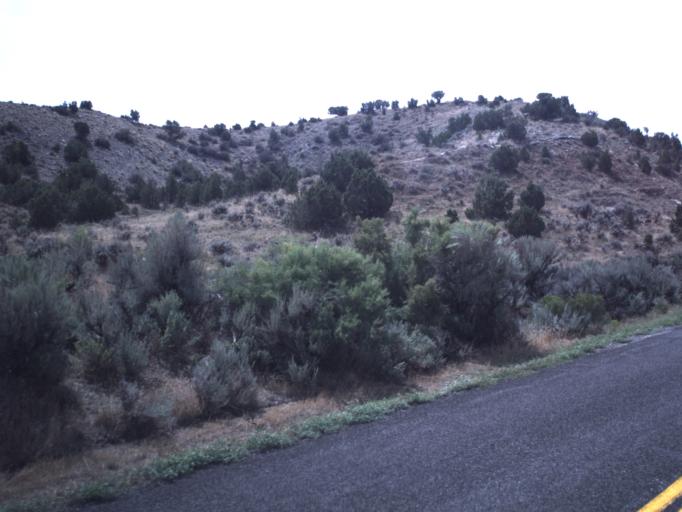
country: US
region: Utah
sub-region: Uintah County
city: Vernal
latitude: 40.5320
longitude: -109.5332
